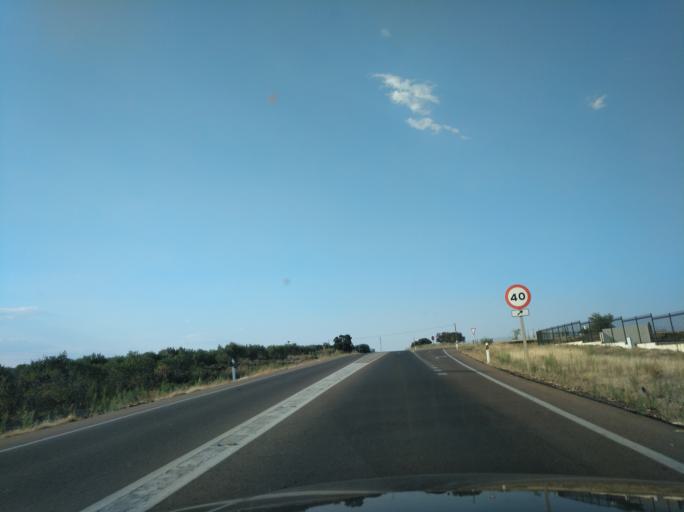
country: ES
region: Extremadura
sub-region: Provincia de Badajoz
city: Olivenza
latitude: 38.7096
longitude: -7.0861
